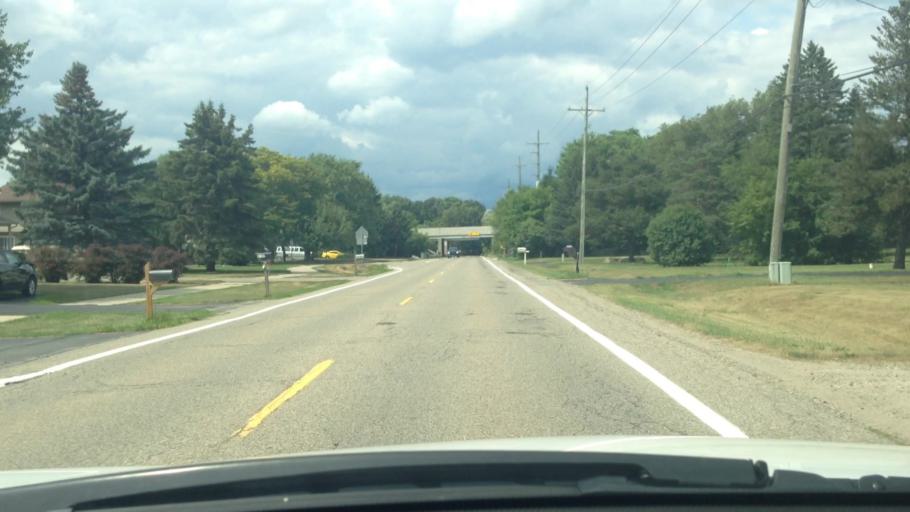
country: US
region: Michigan
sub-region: Oakland County
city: Clarkston
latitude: 42.7431
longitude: -83.3997
